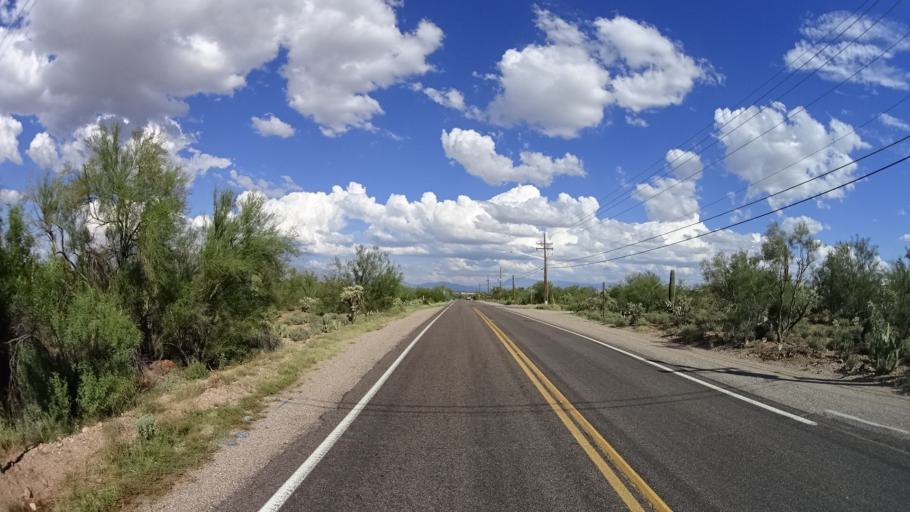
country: US
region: Arizona
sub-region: Pima County
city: Flowing Wells
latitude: 32.2798
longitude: -111.0532
